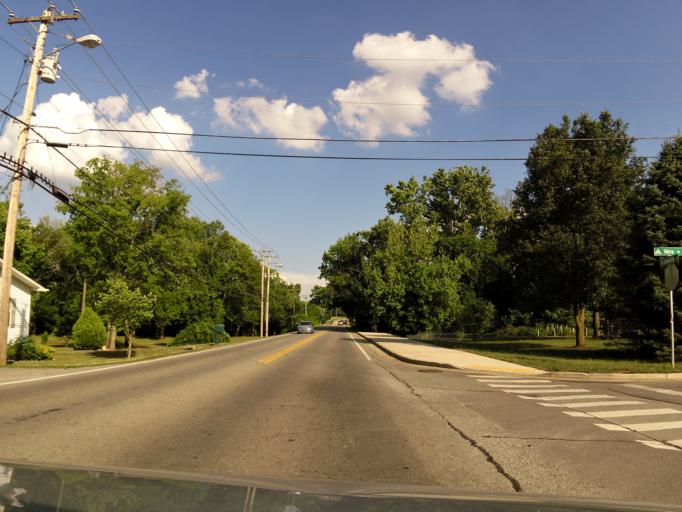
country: US
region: Tennessee
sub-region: Blount County
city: Alcoa
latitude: 35.7788
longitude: -83.9972
